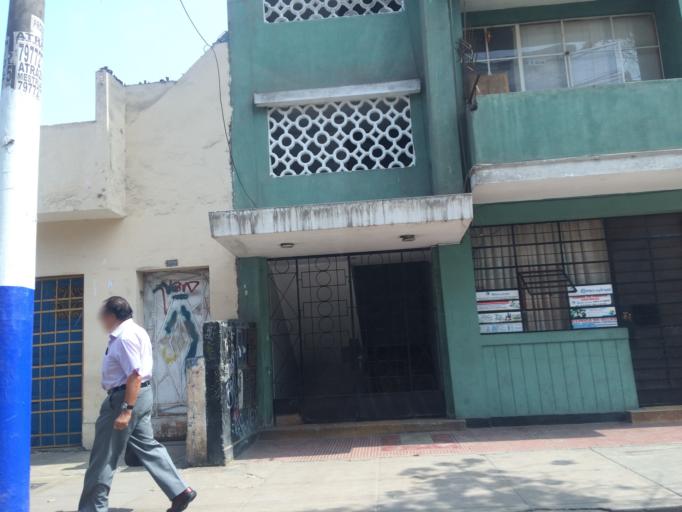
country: PE
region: Lima
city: Lima
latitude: -12.0288
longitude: -77.0355
